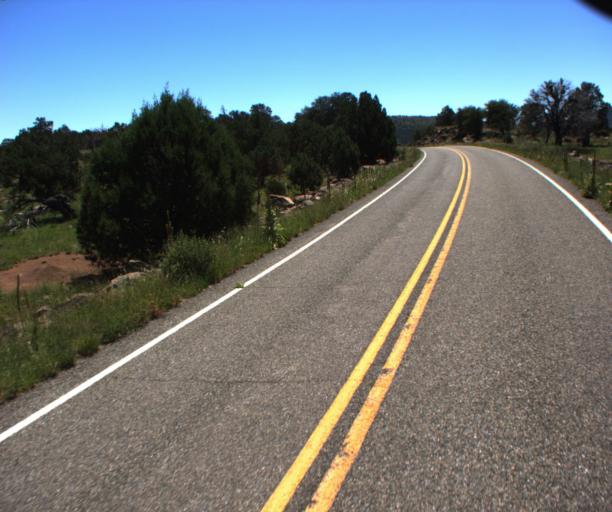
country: US
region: Arizona
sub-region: Greenlee County
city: Morenci
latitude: 33.2948
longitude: -109.3605
